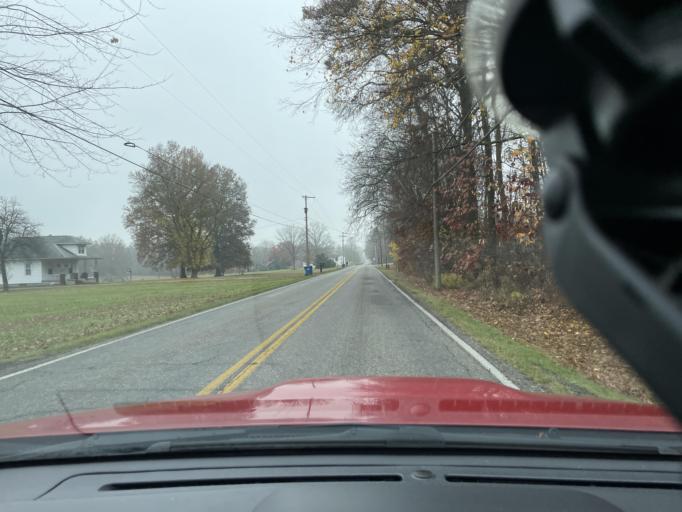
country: US
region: Ohio
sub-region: Trumbull County
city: Mineral Ridge
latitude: 41.1452
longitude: -80.7535
